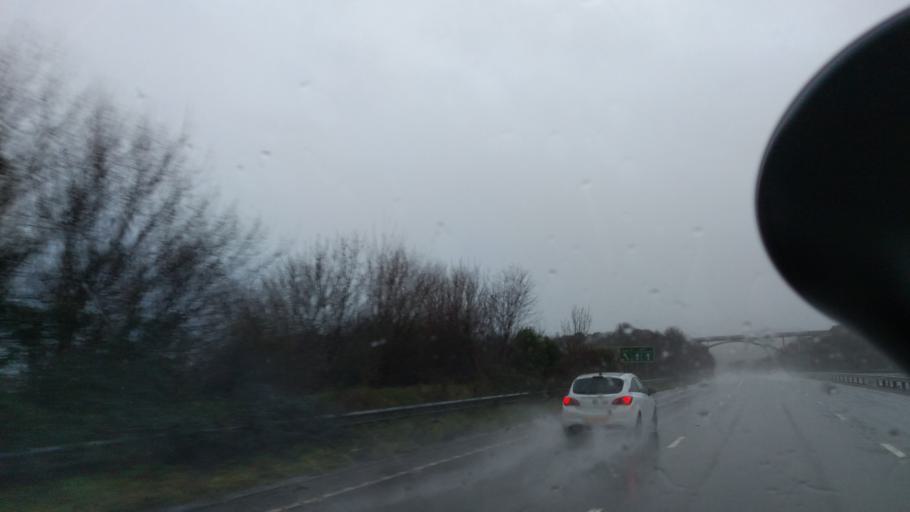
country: GB
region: England
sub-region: West Sussex
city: Shoreham-by-Sea
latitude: 50.8461
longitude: -0.2725
